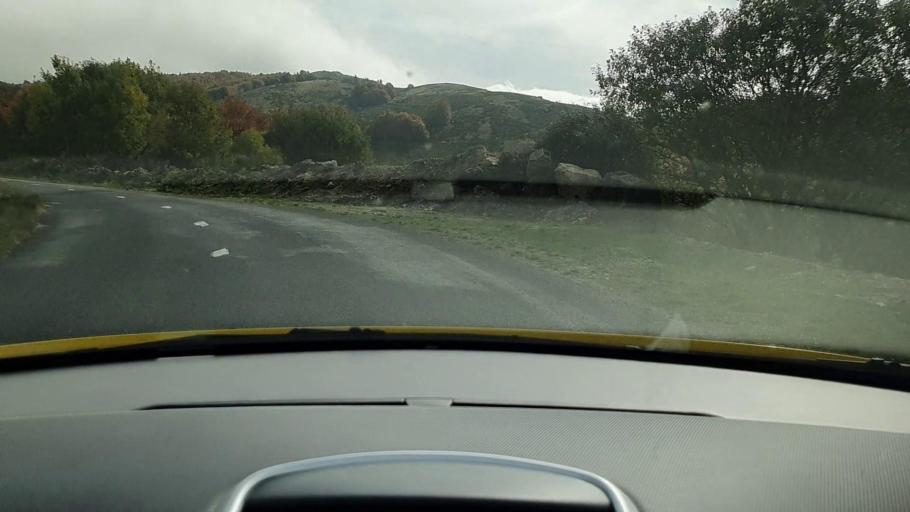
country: FR
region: Languedoc-Roussillon
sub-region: Departement de la Lozere
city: Meyrueis
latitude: 44.0743
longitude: 3.4756
